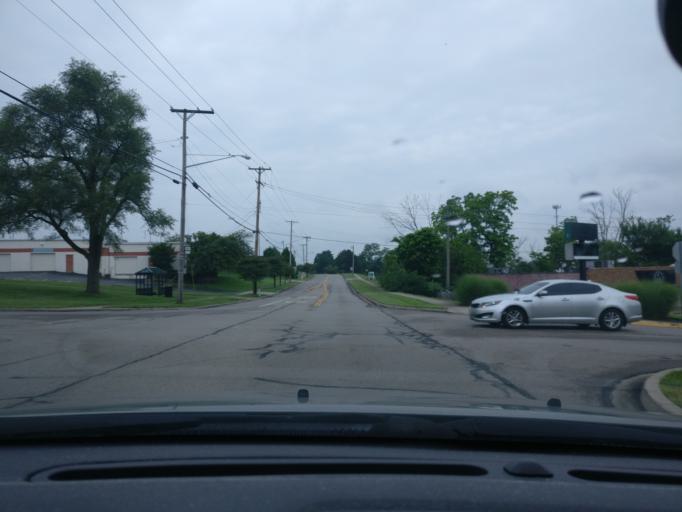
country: US
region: Ohio
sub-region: Montgomery County
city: West Carrollton City
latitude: 39.6411
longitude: -84.2375
